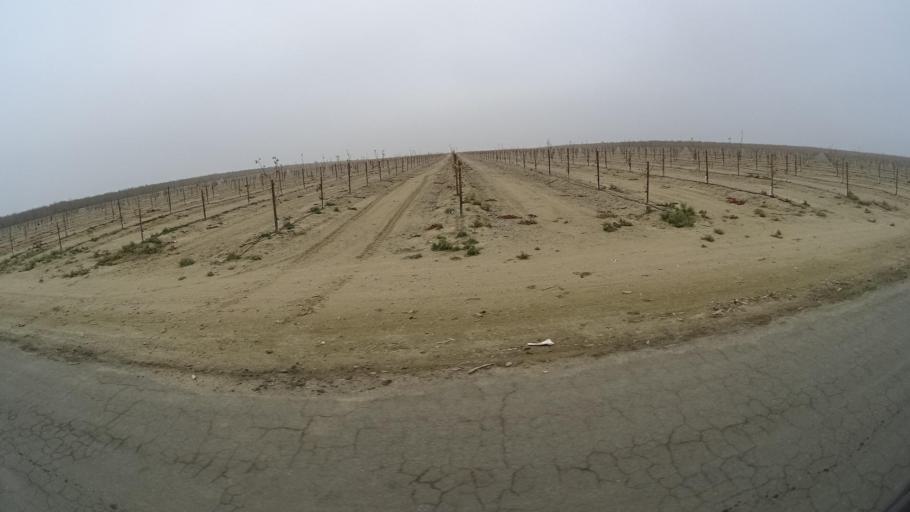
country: US
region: California
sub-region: Kern County
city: Lost Hills
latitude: 35.5720
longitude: -119.5338
